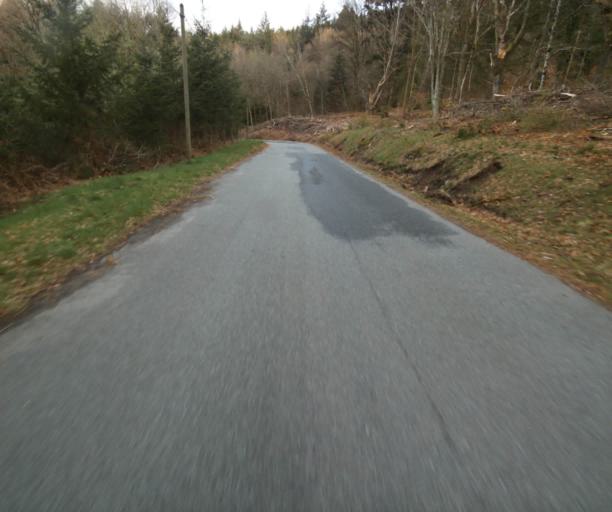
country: FR
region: Limousin
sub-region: Departement de la Correze
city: Correze
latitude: 45.4198
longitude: 1.8875
